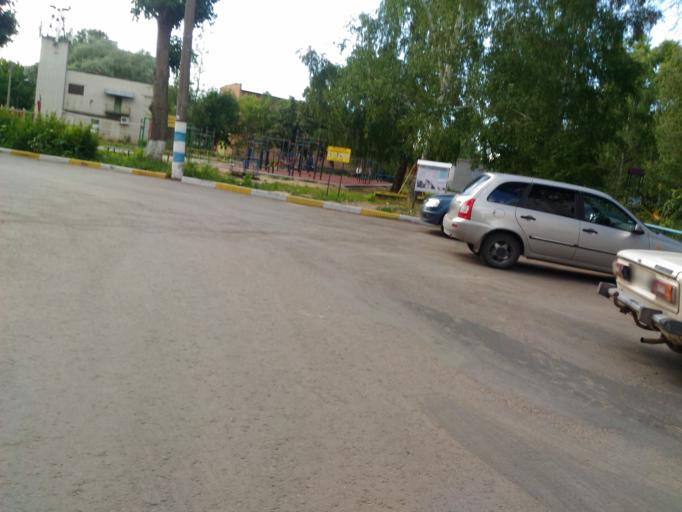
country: RU
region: Ulyanovsk
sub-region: Ulyanovskiy Rayon
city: Ulyanovsk
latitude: 54.3259
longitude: 48.4860
